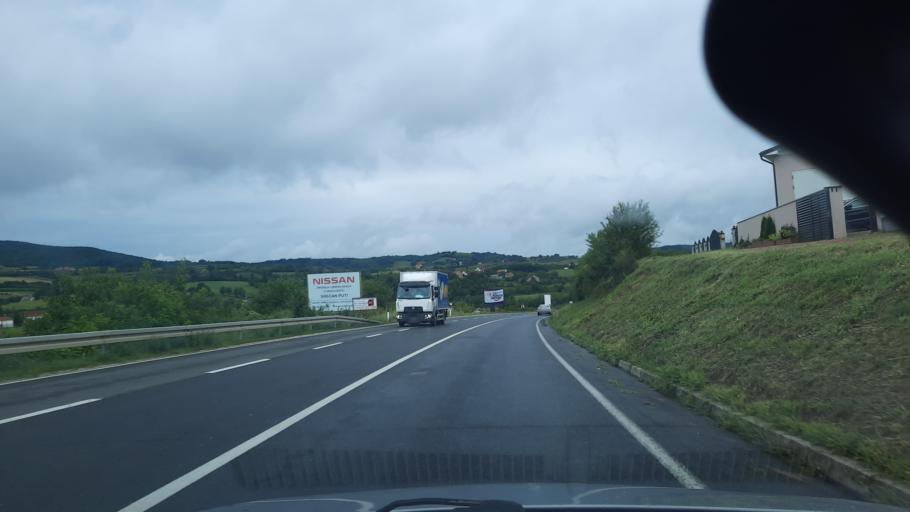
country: RS
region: Central Serbia
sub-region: Sumadijski Okrug
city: Kragujevac
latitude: 43.9786
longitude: 20.8283
